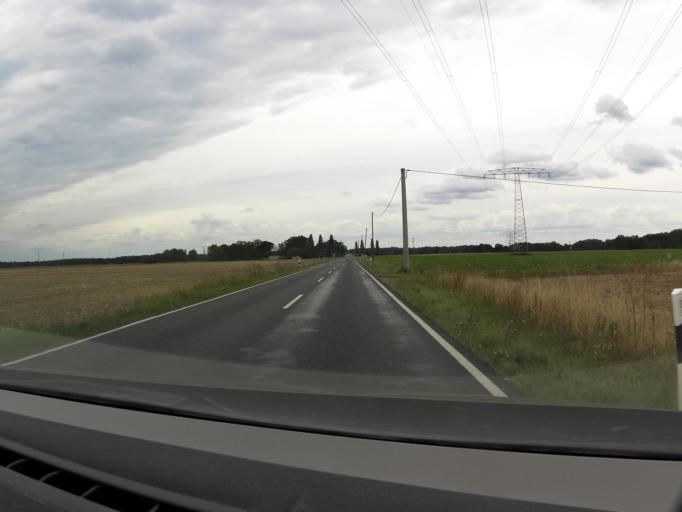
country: DE
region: Saxony-Anhalt
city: Worlitz
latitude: 51.8352
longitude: 12.3909
